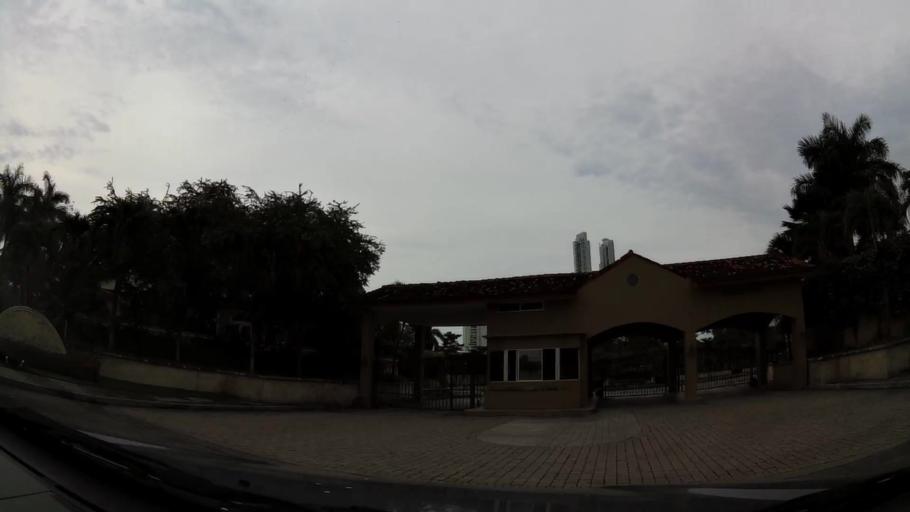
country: PA
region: Panama
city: San Miguelito
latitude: 9.0168
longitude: -79.4602
